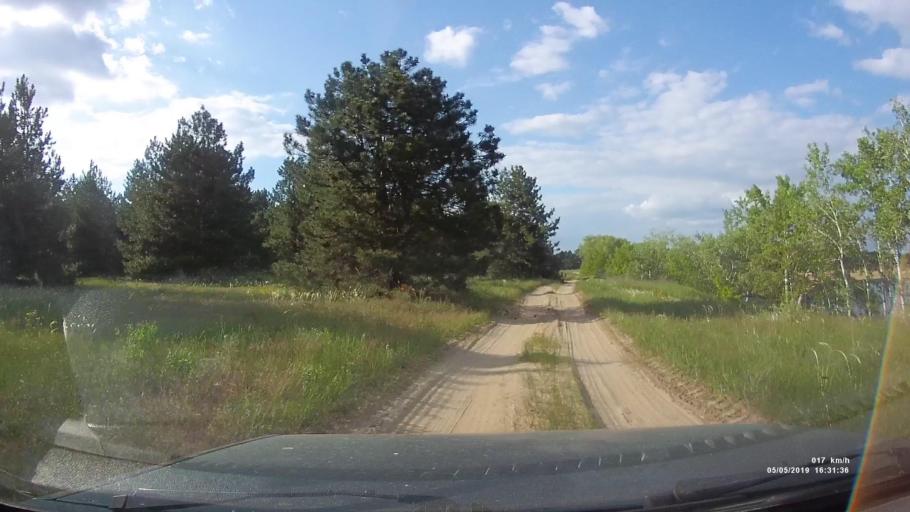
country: RU
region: Rostov
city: Ust'-Donetskiy
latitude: 47.7767
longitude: 41.0145
